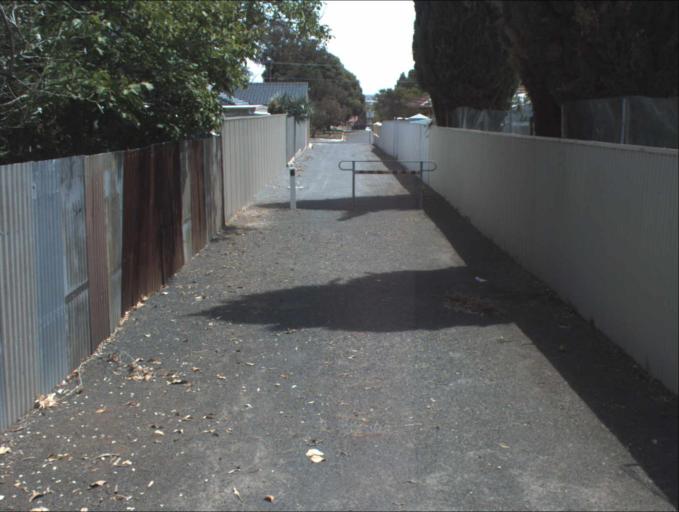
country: AU
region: South Australia
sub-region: Port Adelaide Enfield
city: Enfield
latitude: -34.8514
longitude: 138.6160
